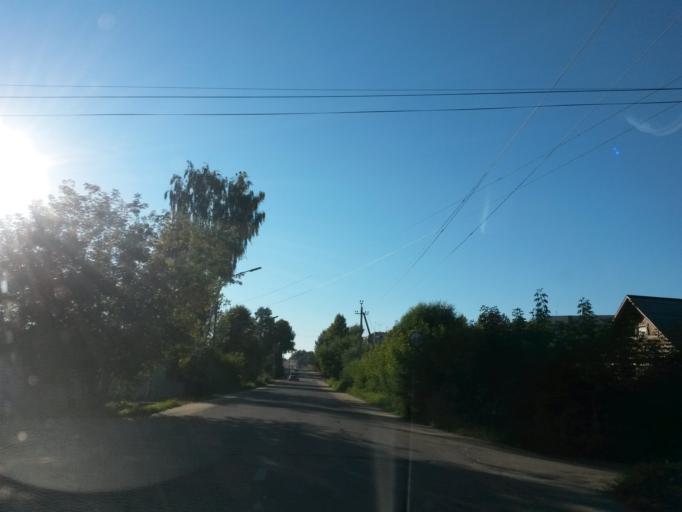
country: RU
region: Jaroslavl
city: Gavrilov-Yam
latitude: 57.2979
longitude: 39.8696
